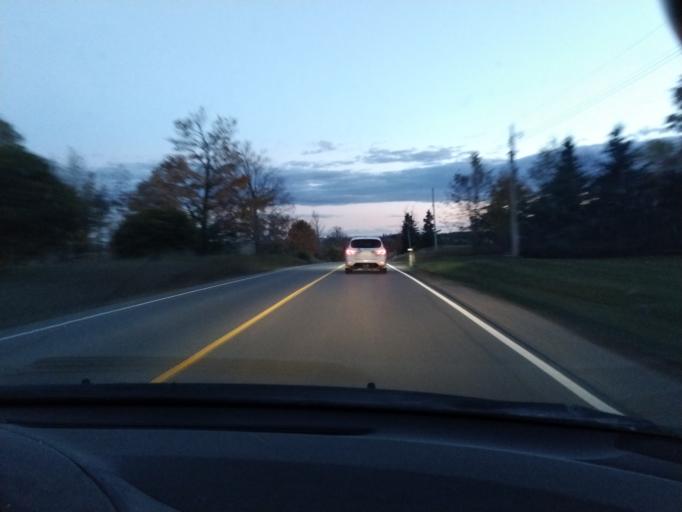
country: CA
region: Ontario
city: Bradford West Gwillimbury
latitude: 44.1410
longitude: -79.6498
